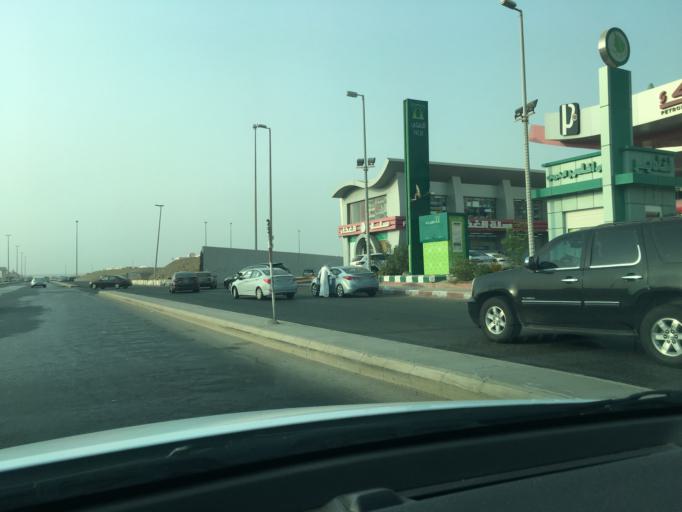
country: SA
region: Makkah
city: Jeddah
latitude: 21.7608
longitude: 39.1838
